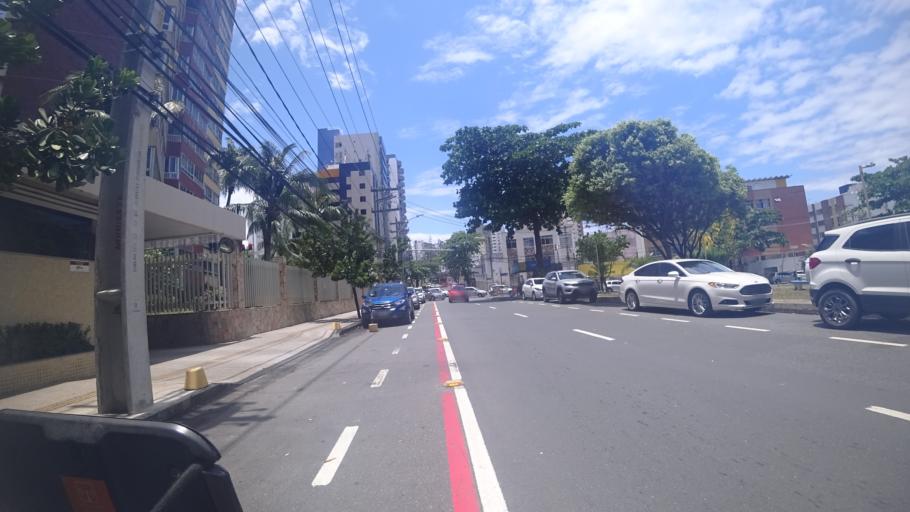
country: BR
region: Bahia
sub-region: Salvador
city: Salvador
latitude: -13.0040
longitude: -38.4595
